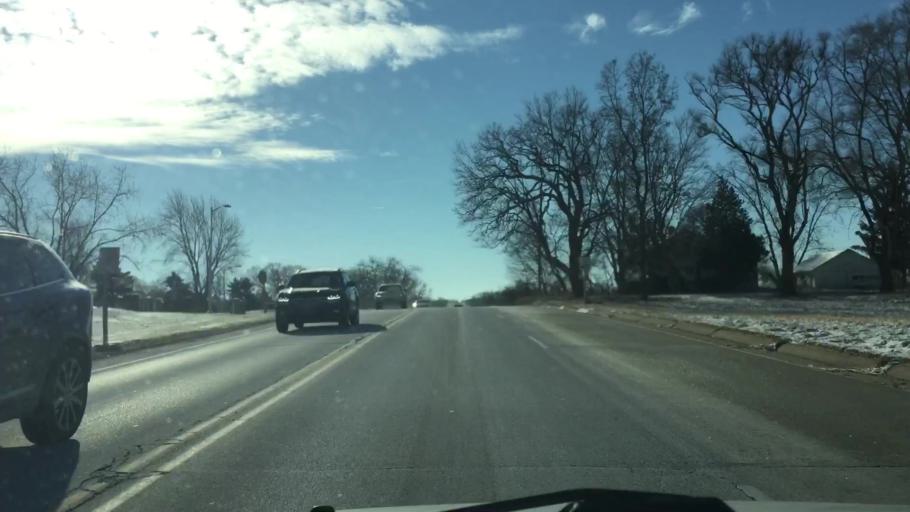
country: US
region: Wisconsin
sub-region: Walworth County
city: Elkhorn
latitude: 42.7131
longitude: -88.5423
